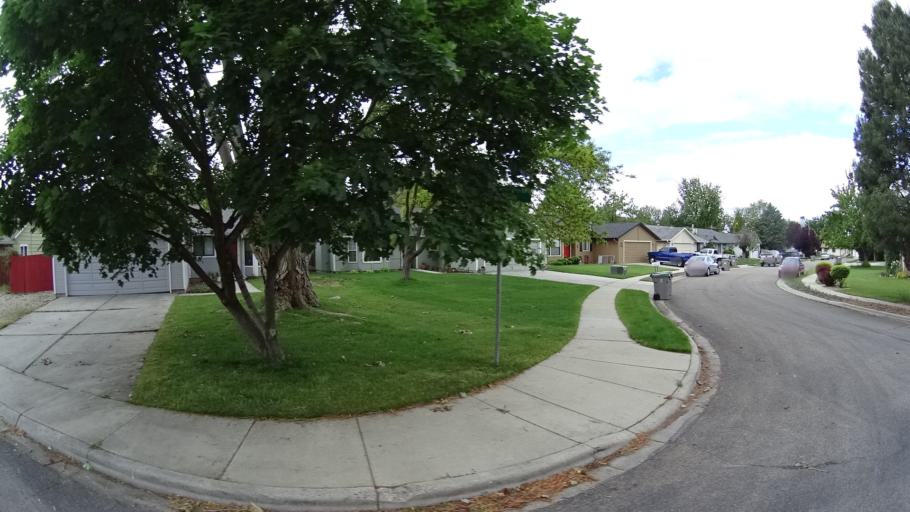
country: US
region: Idaho
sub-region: Ada County
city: Garden City
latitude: 43.6711
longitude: -116.2772
